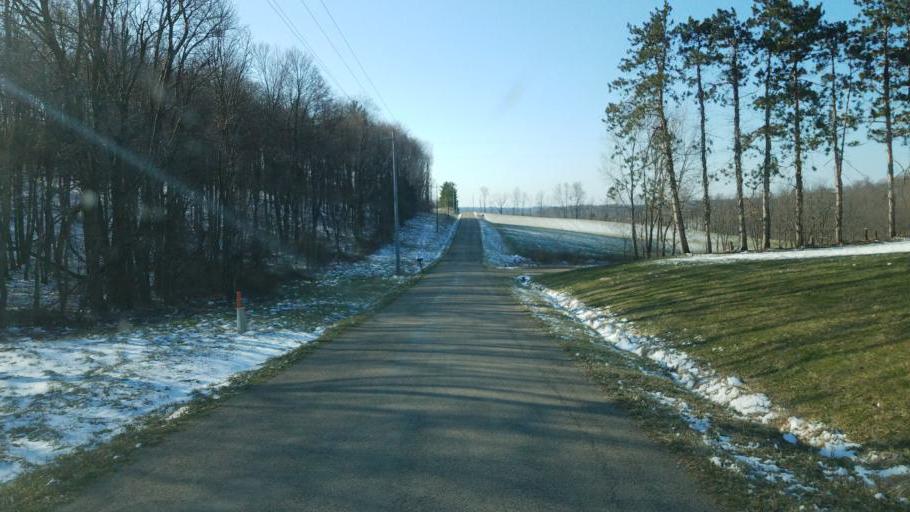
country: US
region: Ohio
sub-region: Sandusky County
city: Bellville
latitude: 40.5764
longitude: -82.4843
